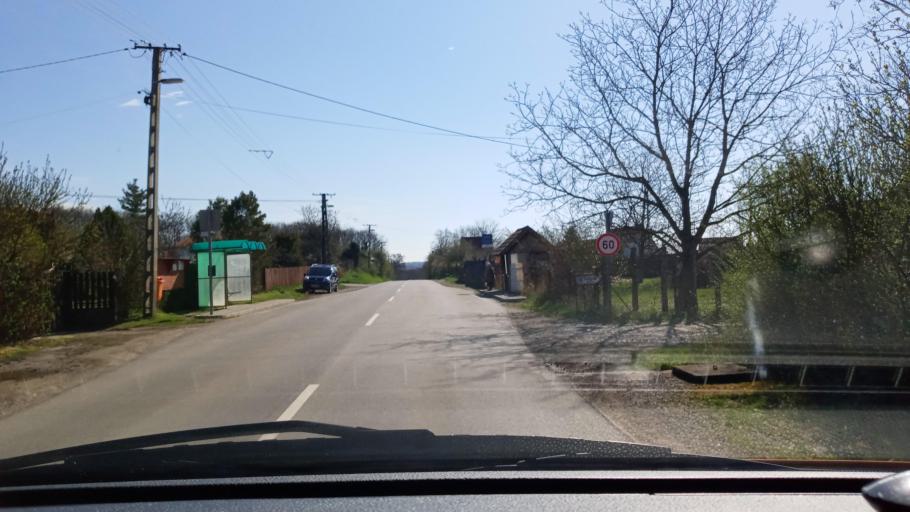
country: HU
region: Baranya
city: Kozarmisleny
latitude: 46.0856
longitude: 18.2997
